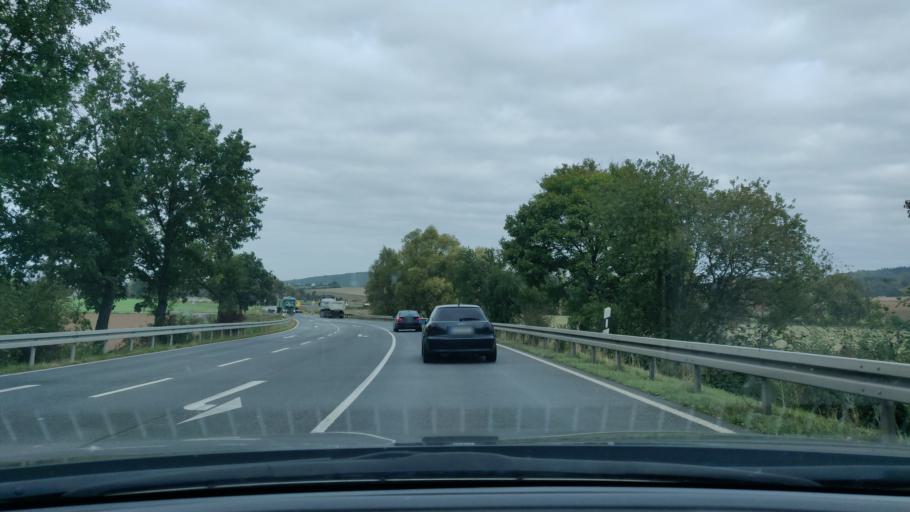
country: DE
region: Hesse
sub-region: Regierungsbezirk Kassel
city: Homberg
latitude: 51.0514
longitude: 9.3864
